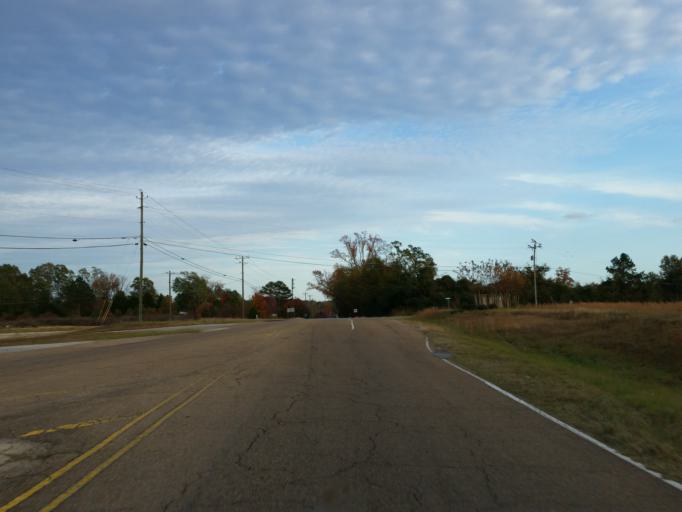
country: US
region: Mississippi
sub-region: Lauderdale County
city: Marion
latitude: 32.4123
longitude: -88.6202
